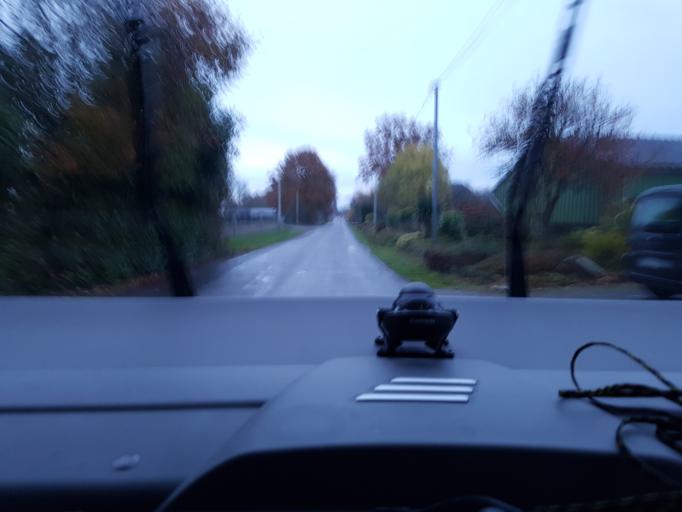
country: FR
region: Brittany
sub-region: Departement d'Ille-et-Vilaine
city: Livre-sur-Changeon
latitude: 48.2400
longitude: -1.3172
